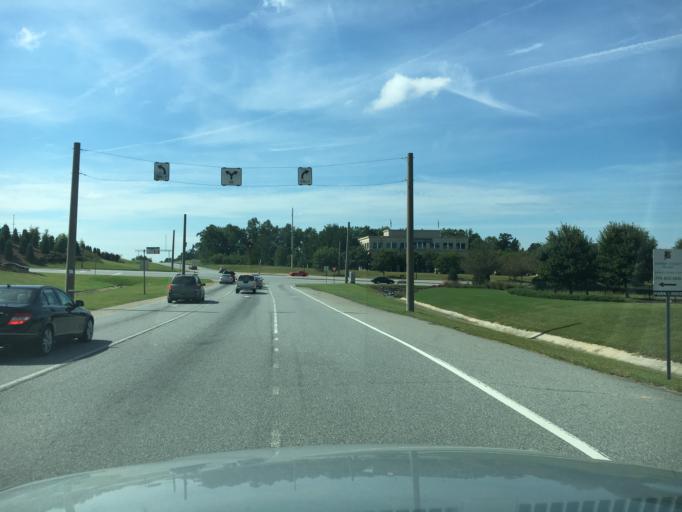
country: US
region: Georgia
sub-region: Gwinnett County
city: Duluth
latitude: 33.9892
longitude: -84.0847
